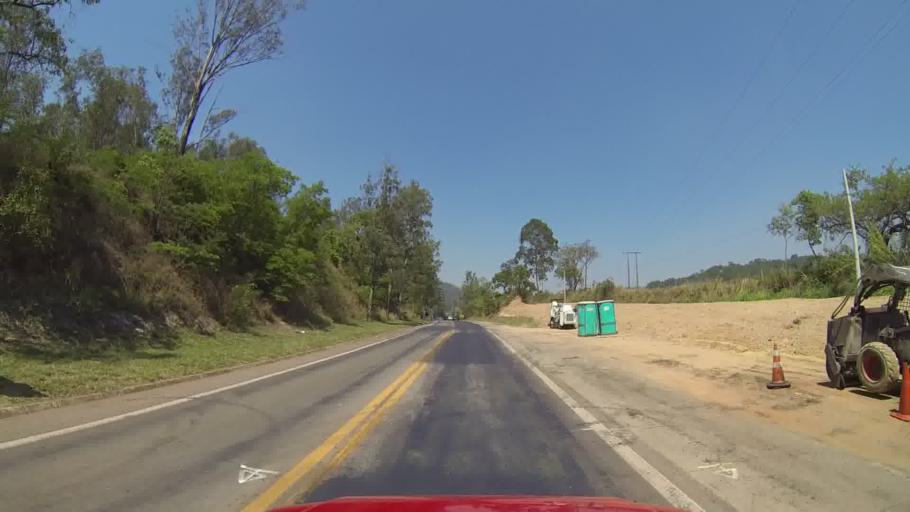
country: BR
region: Minas Gerais
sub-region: Mateus Leme
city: Mateus Leme
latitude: -20.0212
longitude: -44.4993
